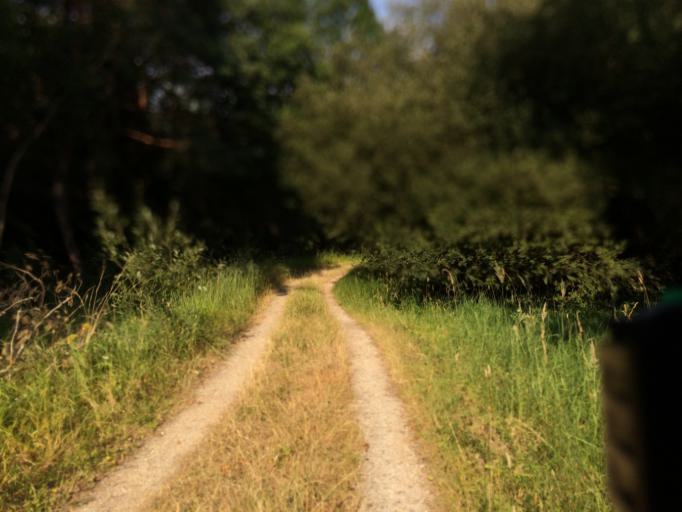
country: FR
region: Ile-de-France
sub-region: Departement de l'Essonne
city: Tigery
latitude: 48.6667
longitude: 2.4946
